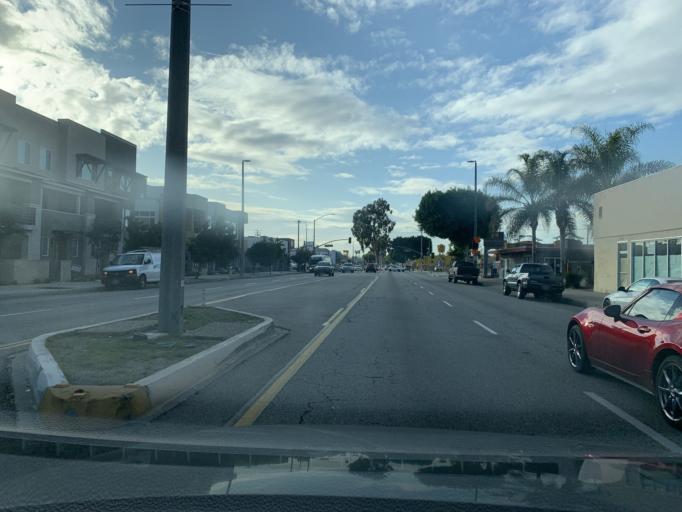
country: US
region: California
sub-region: Los Angeles County
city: El Monte
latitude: 34.0629
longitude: -118.0343
